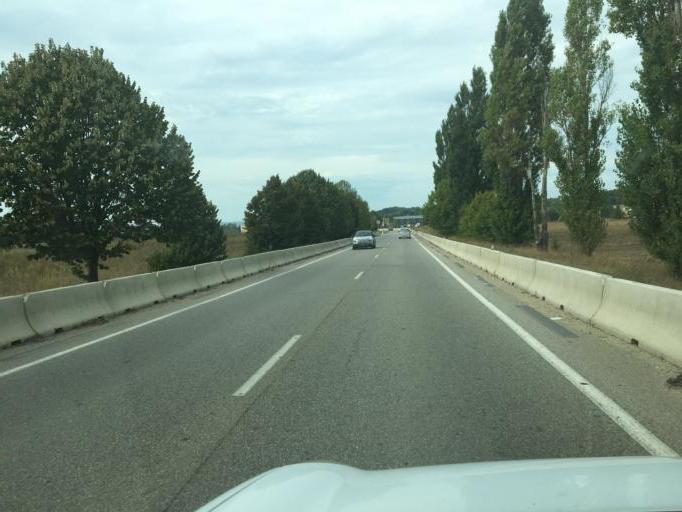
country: FR
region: Provence-Alpes-Cote d'Azur
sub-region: Departement des Bouches-du-Rhone
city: Bouc-Bel-Air
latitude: 43.4751
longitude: 5.3982
